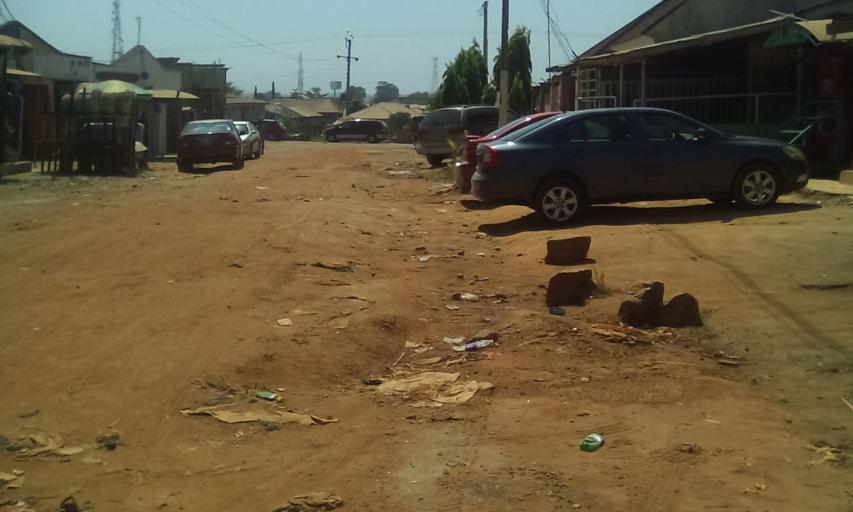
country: NG
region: Abuja Federal Capital Territory
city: Abuja
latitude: 8.9846
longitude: 7.3710
